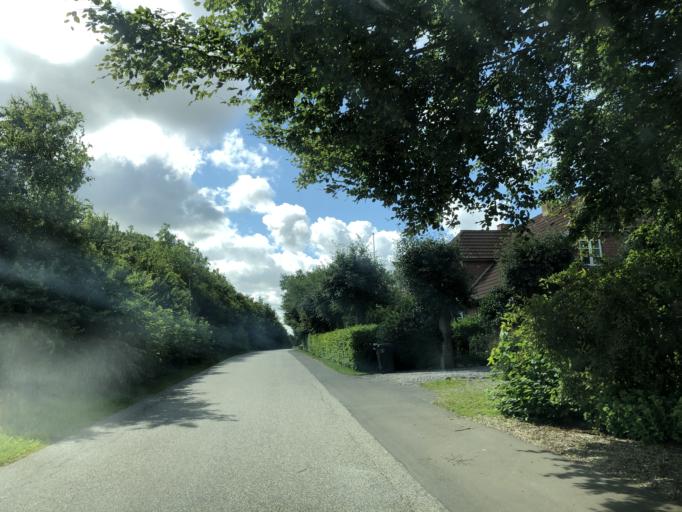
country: DK
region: Central Jutland
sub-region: Struer Kommune
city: Struer
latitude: 56.4637
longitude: 8.5226
